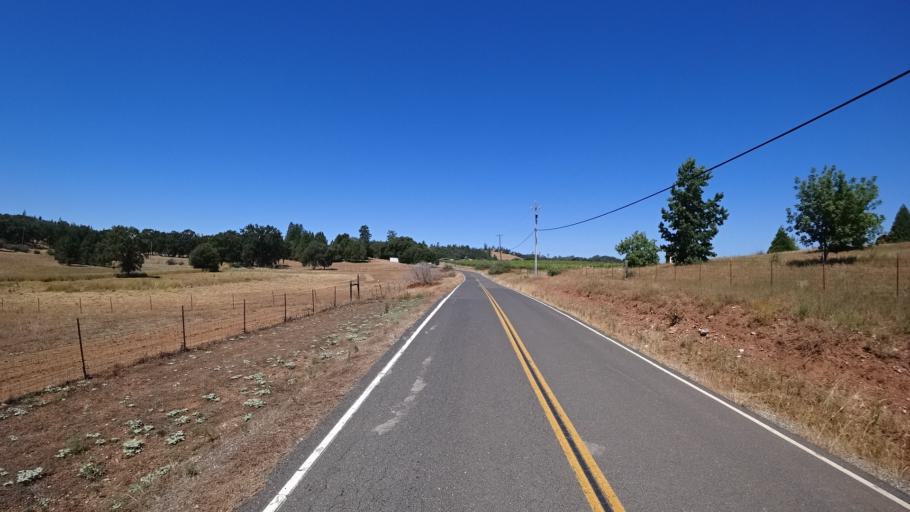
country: US
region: California
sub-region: Calaveras County
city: Mountain Ranch
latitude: 38.2154
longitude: -120.5392
